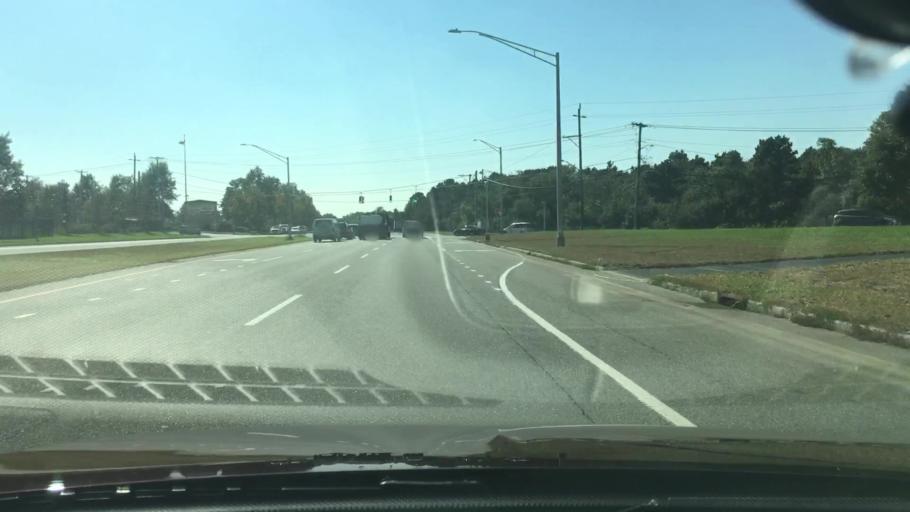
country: US
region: New York
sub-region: Suffolk County
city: North Bellport
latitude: 40.8111
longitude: -72.9532
